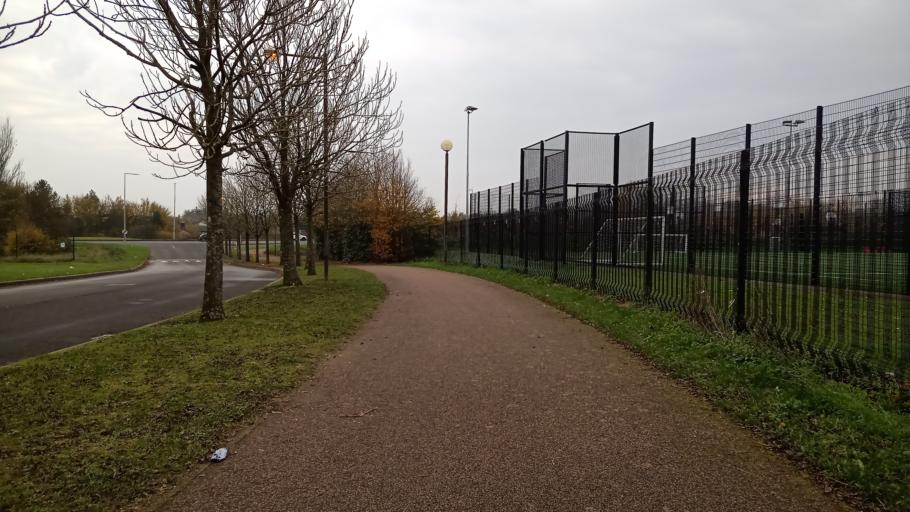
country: GB
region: England
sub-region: Milton Keynes
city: Shenley Church End
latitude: 52.0078
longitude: -0.7870
